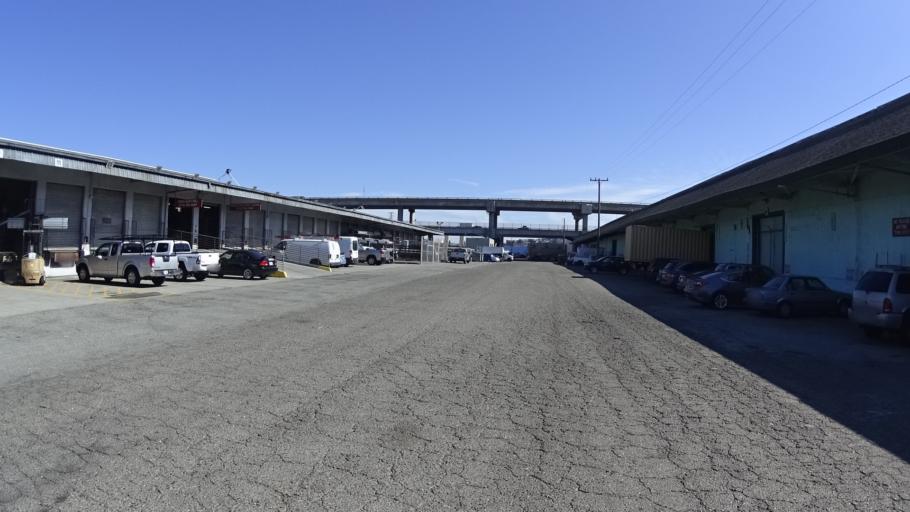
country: US
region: California
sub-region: San Francisco County
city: San Francisco
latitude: 37.7452
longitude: -122.3974
